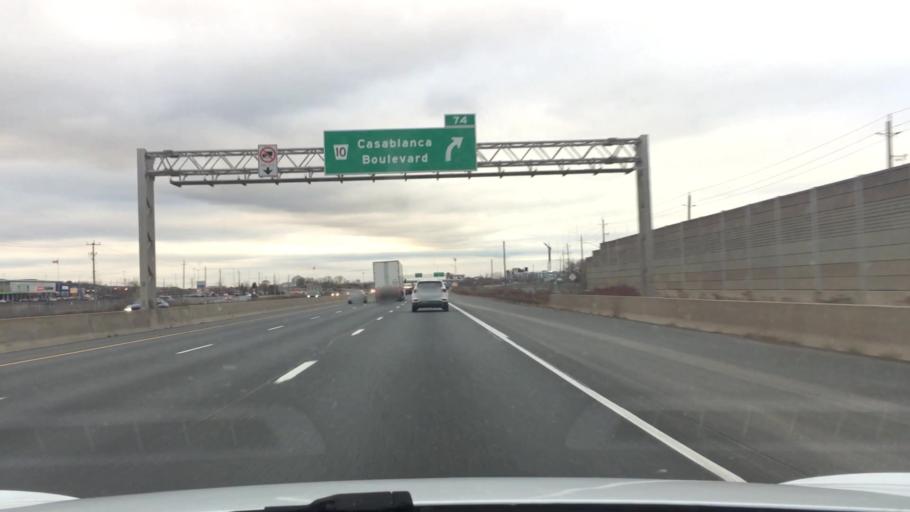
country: CA
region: Ontario
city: Oakville
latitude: 43.2045
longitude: -79.5845
